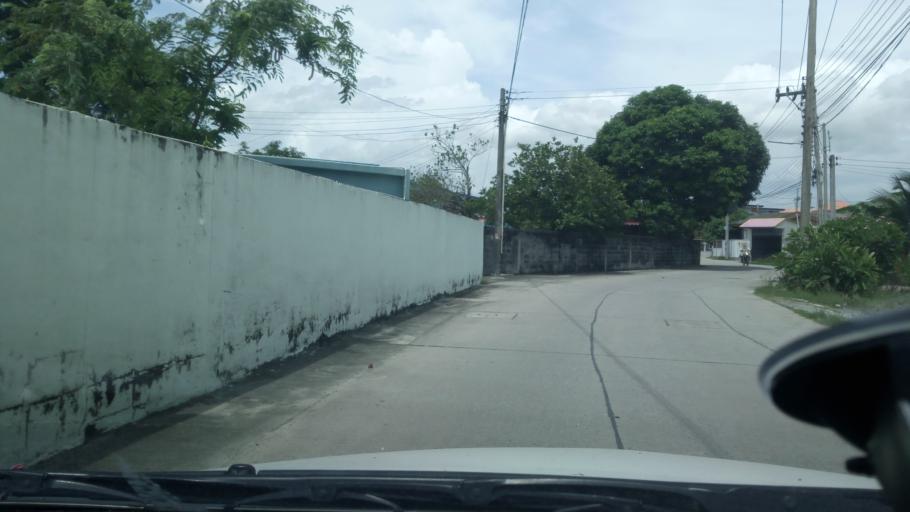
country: TH
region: Chon Buri
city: Phan Thong
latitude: 13.4144
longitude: 101.0505
